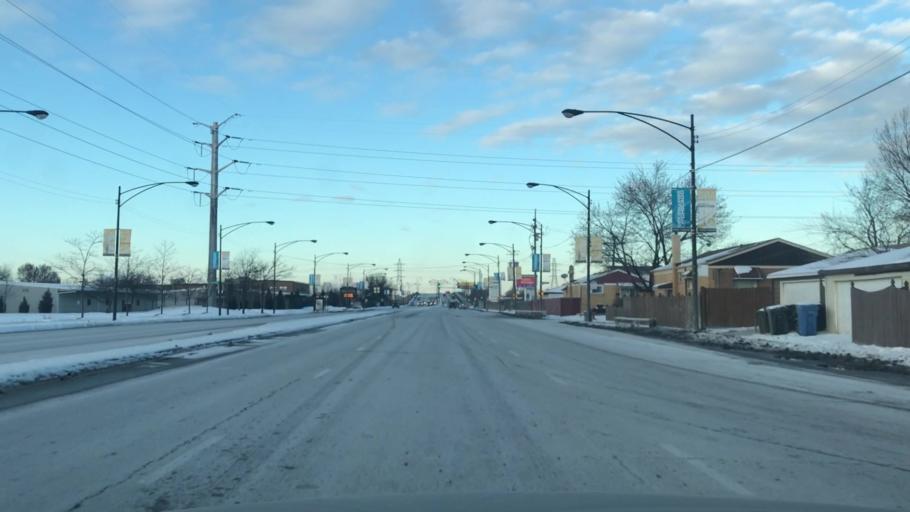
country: US
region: Illinois
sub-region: Cook County
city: Hometown
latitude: 41.7558
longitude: -87.7221
